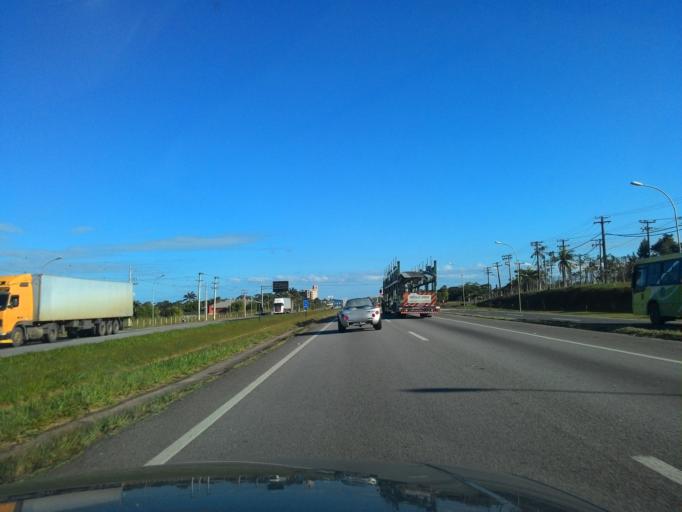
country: BR
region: Sao Paulo
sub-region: Registro
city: Registro
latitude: -24.5202
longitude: -47.8536
